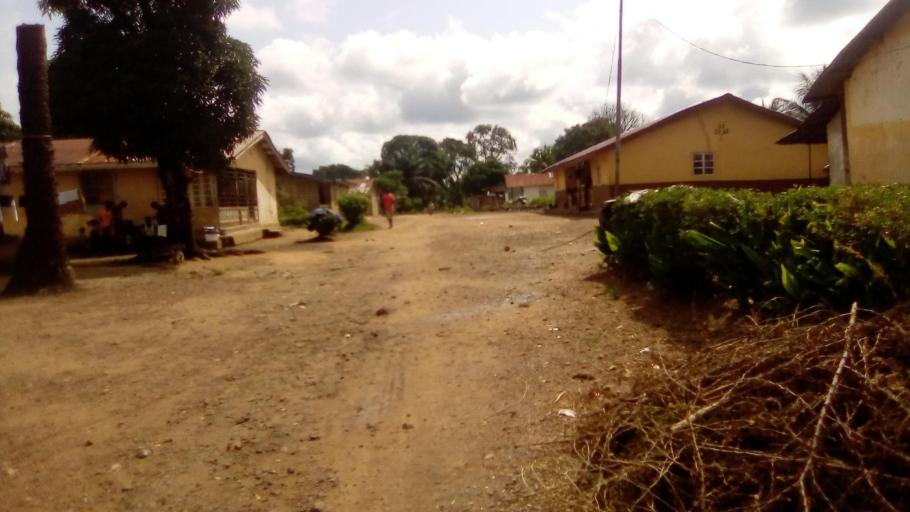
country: SL
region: Southern Province
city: Bo
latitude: 7.9778
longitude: -11.7269
